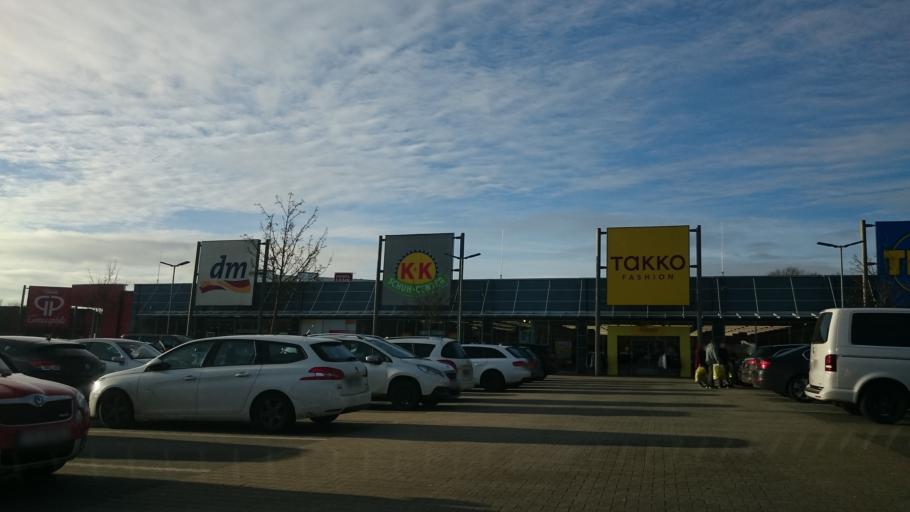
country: DE
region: Saxony
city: Zwickau
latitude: 50.7076
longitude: 12.5010
